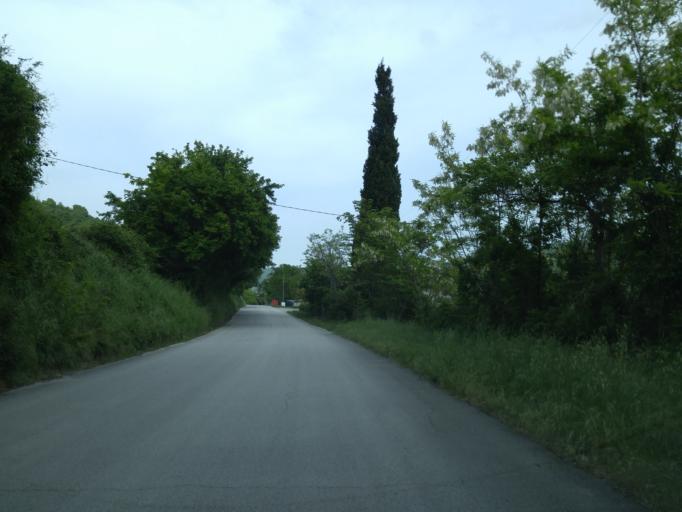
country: IT
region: The Marches
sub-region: Provincia di Pesaro e Urbino
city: Canavaccio
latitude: 43.6634
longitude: 12.7402
